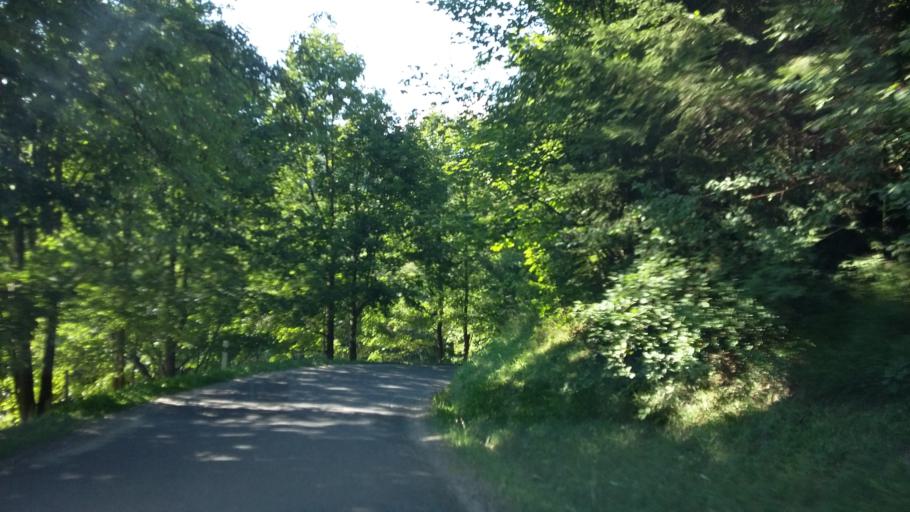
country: CZ
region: Liberecky
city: Mala Skala
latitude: 50.6087
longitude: 15.1922
